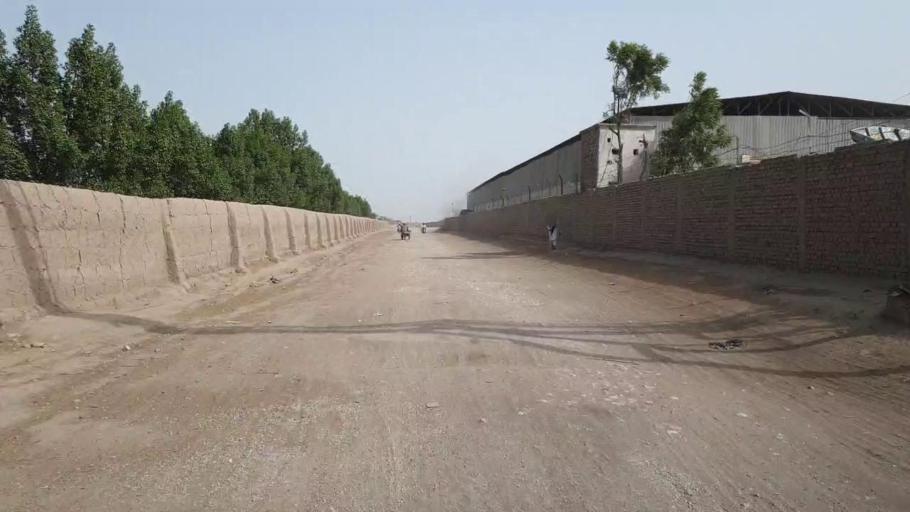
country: PK
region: Sindh
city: Daulatpur
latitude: 26.5579
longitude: 67.9890
